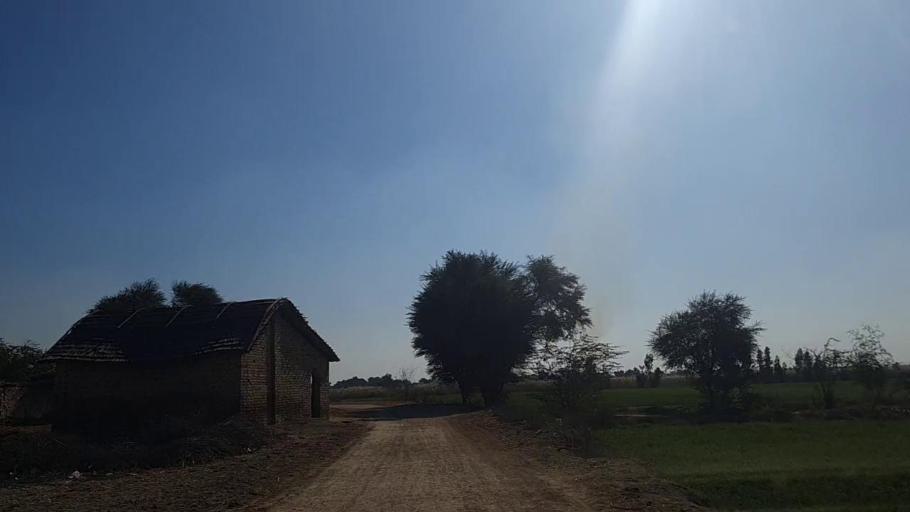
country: PK
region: Sindh
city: Sakrand
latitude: 26.2510
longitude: 68.1925
